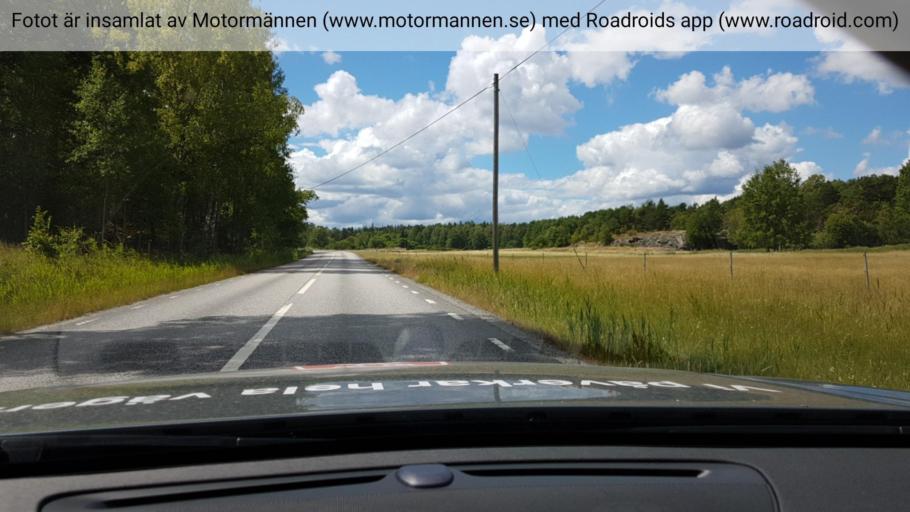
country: SE
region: Stockholm
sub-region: Varmdo Kommun
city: Hemmesta
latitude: 59.3954
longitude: 18.4760
